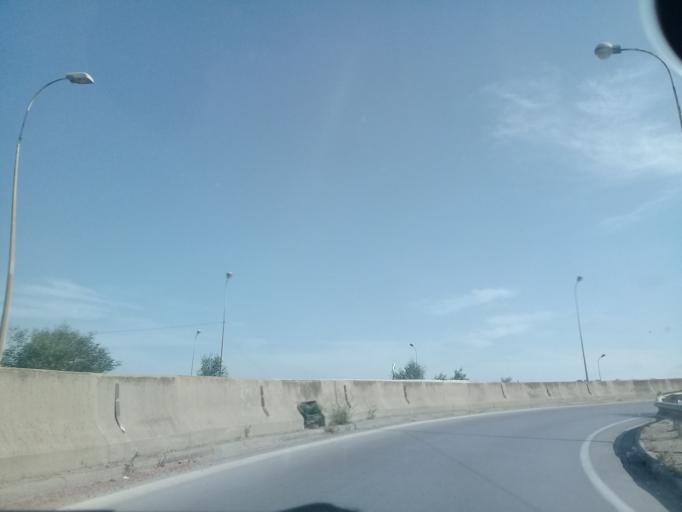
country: TN
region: Ariana
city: Ariana
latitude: 36.8253
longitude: 10.2013
